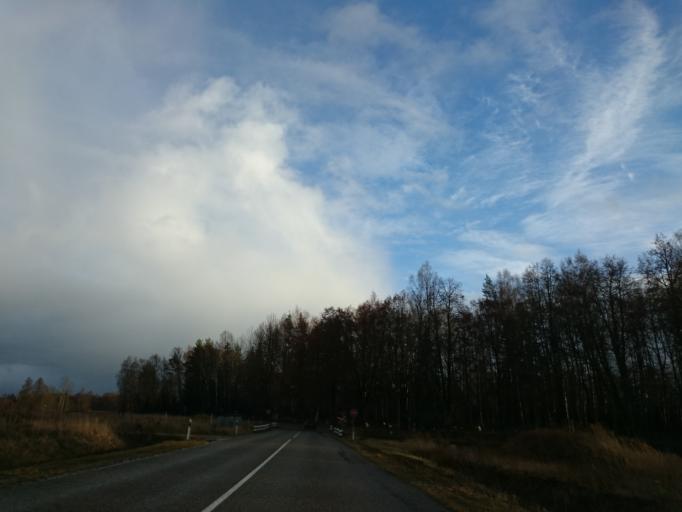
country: LV
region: Skrunda
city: Skrunda
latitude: 56.6805
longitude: 21.9203
